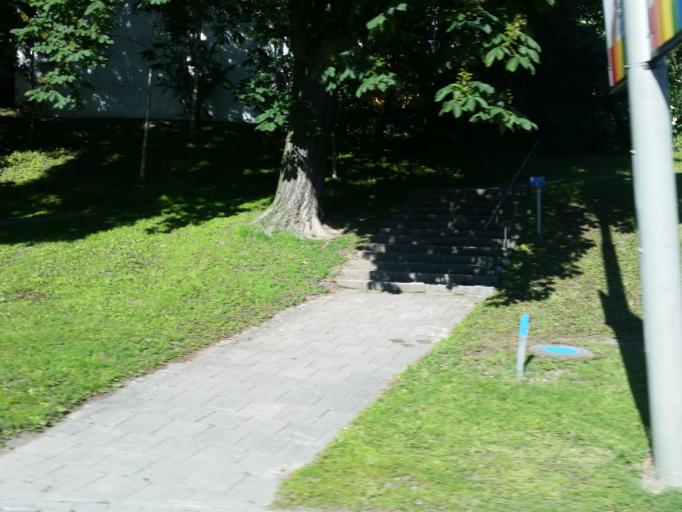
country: SE
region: Stockholm
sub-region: Stockholms Kommun
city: Stockholm
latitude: 59.3480
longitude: 18.0520
